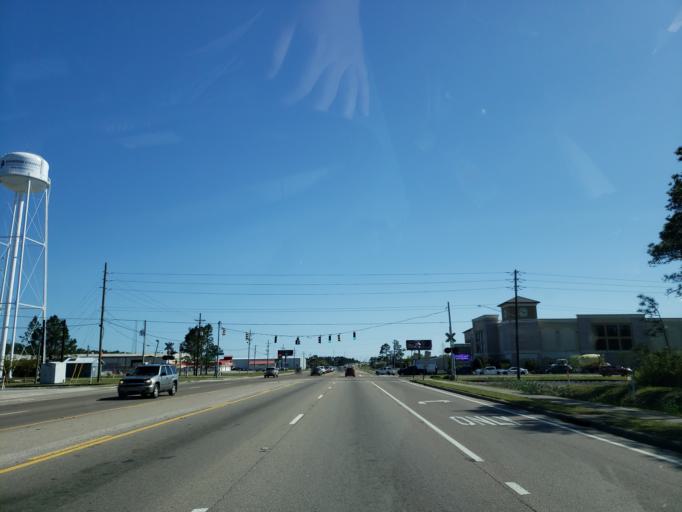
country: US
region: Mississippi
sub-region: Harrison County
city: West Gulfport
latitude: 30.4354
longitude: -89.0313
